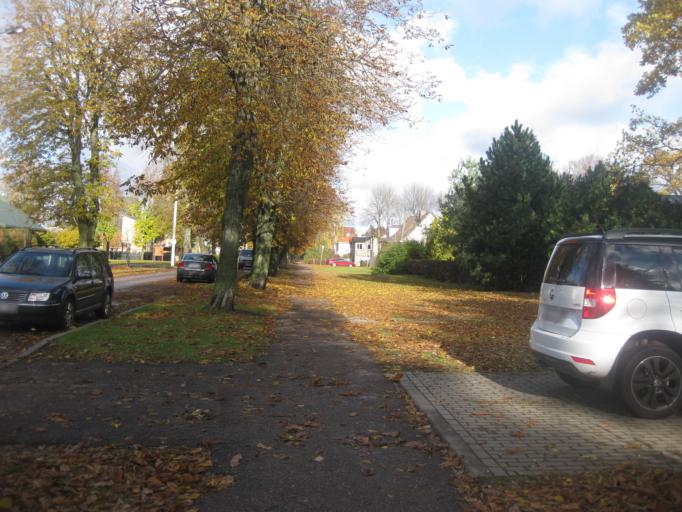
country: LT
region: Kauno apskritis
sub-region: Kaunas
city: Eiguliai
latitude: 54.9033
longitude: 23.9404
